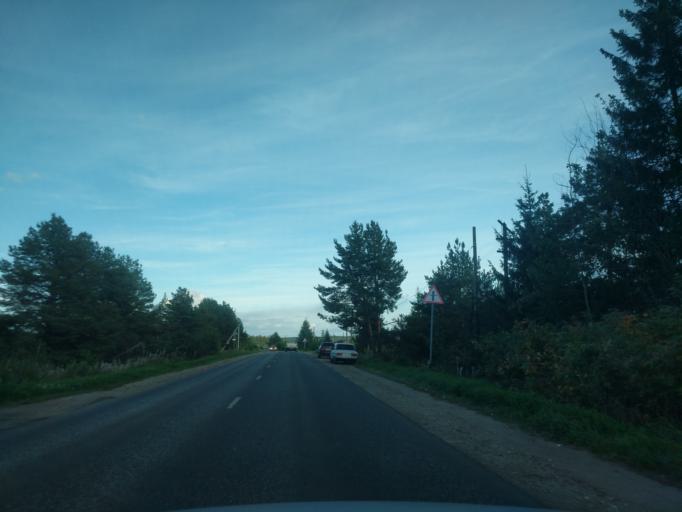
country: RU
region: Kirov
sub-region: Kirovo-Chepetskiy Rayon
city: Kirov
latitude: 58.6032
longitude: 49.8190
